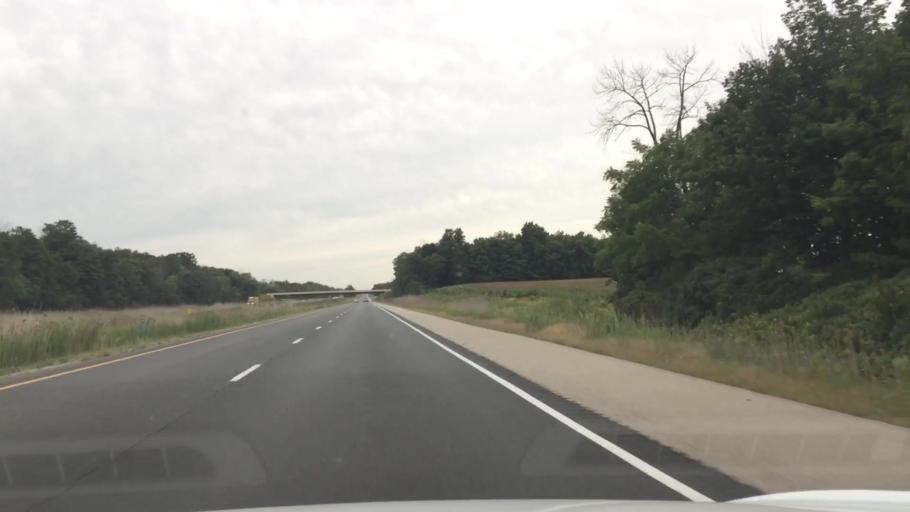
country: CA
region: Ontario
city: Lambton Shores
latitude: 42.9924
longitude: -81.8261
